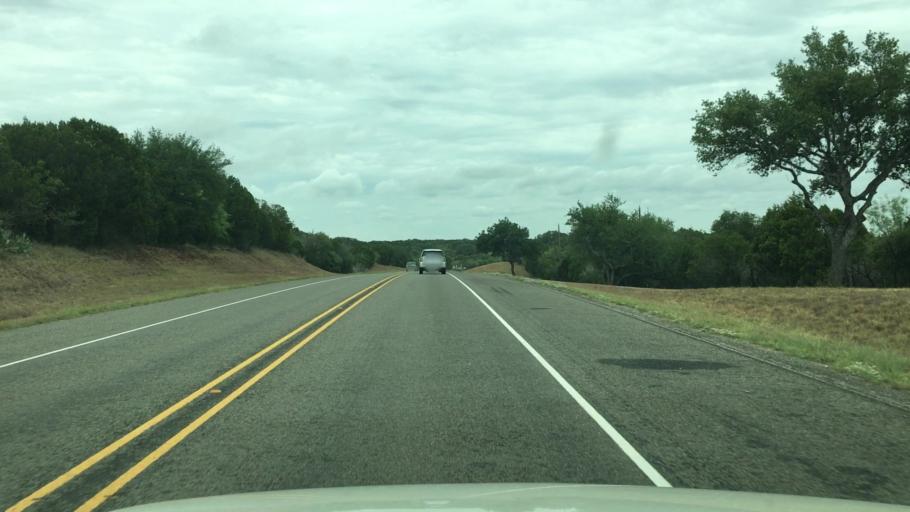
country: US
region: Texas
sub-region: Burnet County
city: Granite Shoals
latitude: 30.5426
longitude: -98.4528
